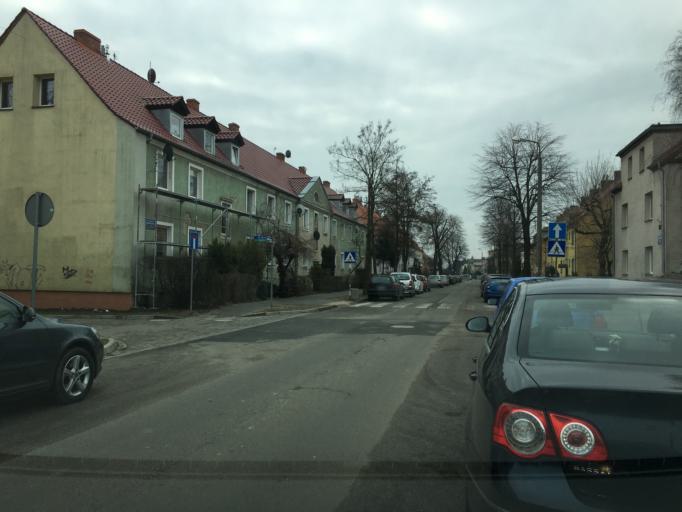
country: PL
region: Opole Voivodeship
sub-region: Powiat kedzierzynsko-kozielski
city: Kedzierzyn-Kozle
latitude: 50.3427
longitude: 18.2129
